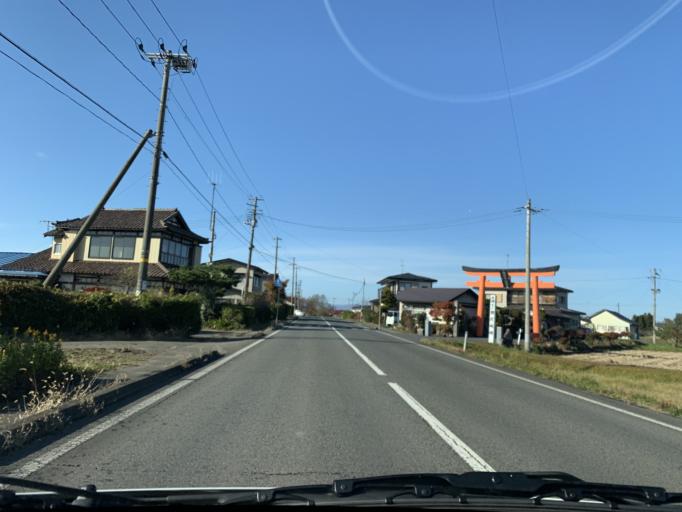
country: JP
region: Iwate
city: Mizusawa
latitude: 39.1816
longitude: 141.1314
